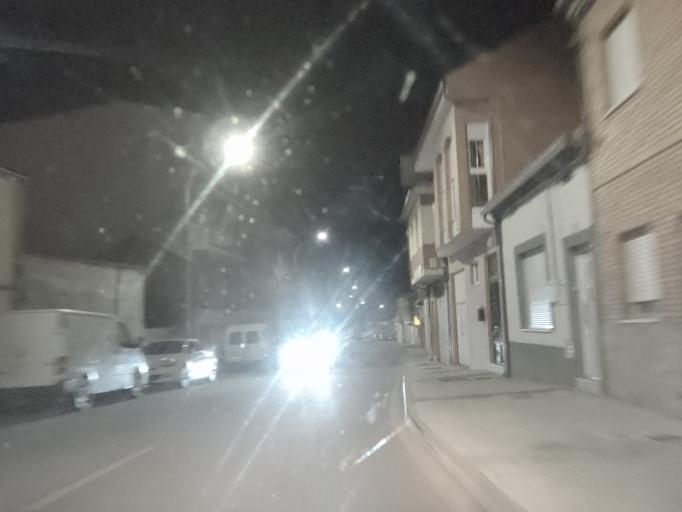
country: ES
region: Castille and Leon
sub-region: Provincia de Zamora
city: Benavente
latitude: 41.9980
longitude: -5.6790
